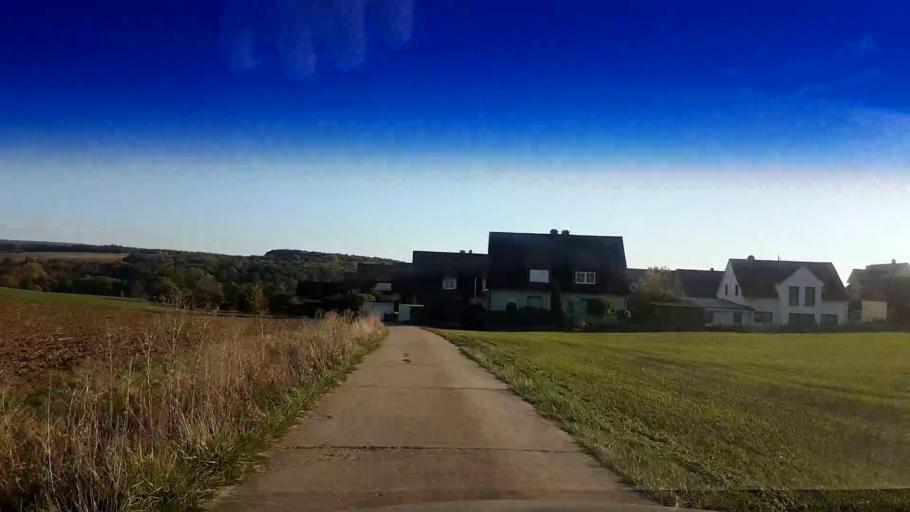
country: DE
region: Bavaria
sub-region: Upper Franconia
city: Memmelsdorf
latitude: 49.9492
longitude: 10.9750
